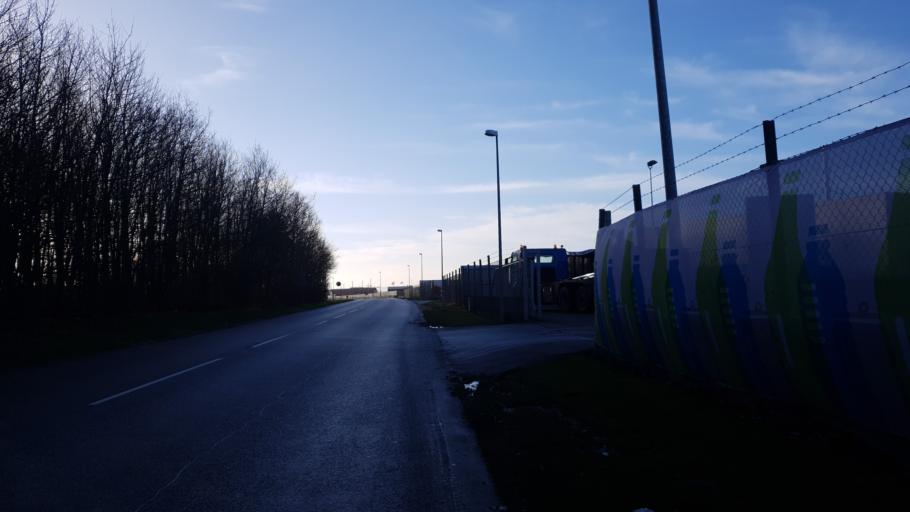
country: DK
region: Central Jutland
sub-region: Hedensted Kommune
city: Hedensted
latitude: 55.8001
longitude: 9.6768
